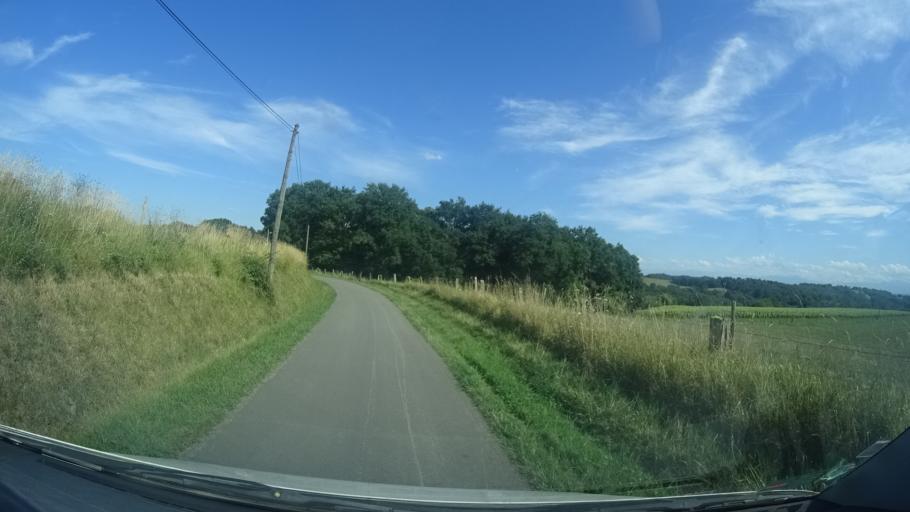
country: FR
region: Aquitaine
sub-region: Departement des Pyrenees-Atlantiques
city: Orthez
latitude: 43.5071
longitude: -0.7023
